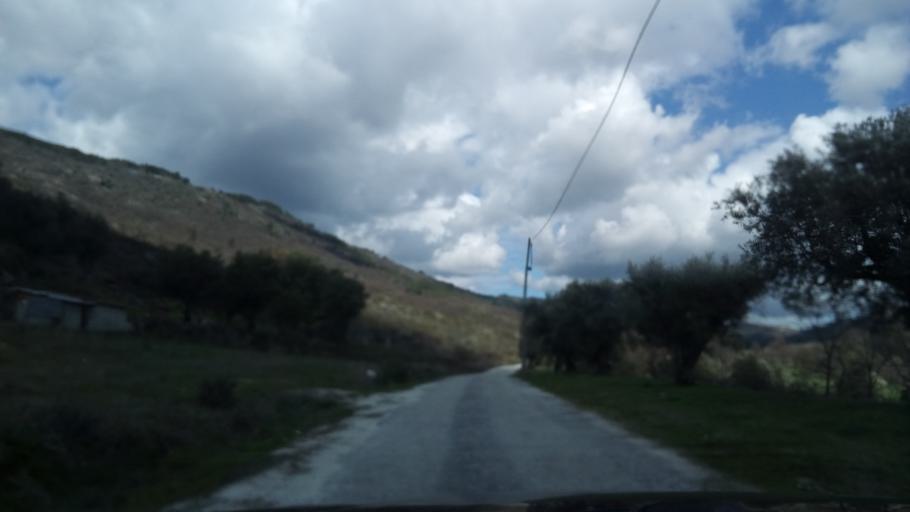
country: PT
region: Guarda
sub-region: Fornos de Algodres
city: Fornos de Algodres
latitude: 40.6402
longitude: -7.5092
